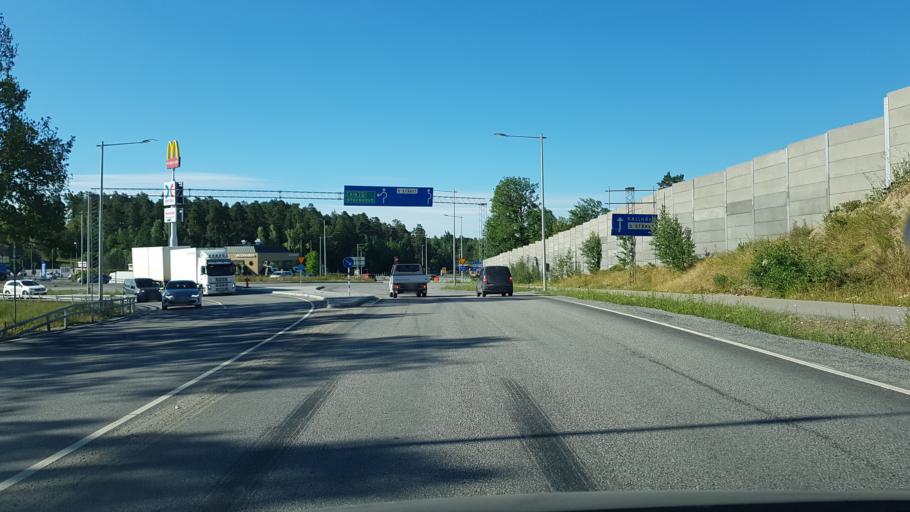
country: SE
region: Stockholm
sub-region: Jarfalla Kommun
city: Jakobsberg
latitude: 59.4711
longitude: 17.8102
